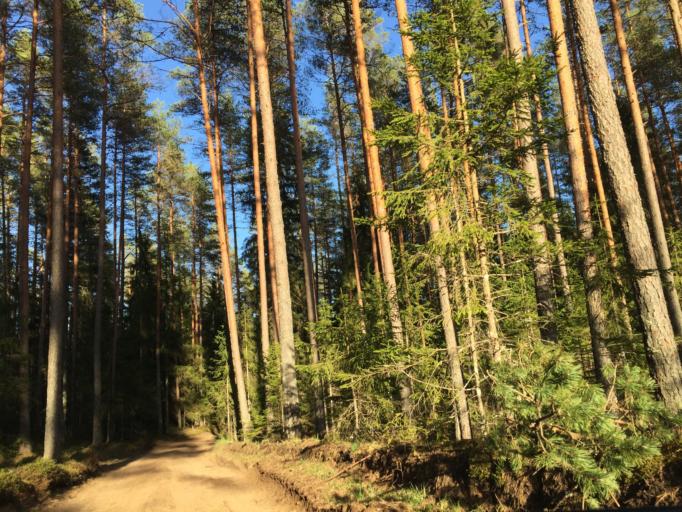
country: LV
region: Valkas Rajons
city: Valka
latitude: 57.7973
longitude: 25.9595
